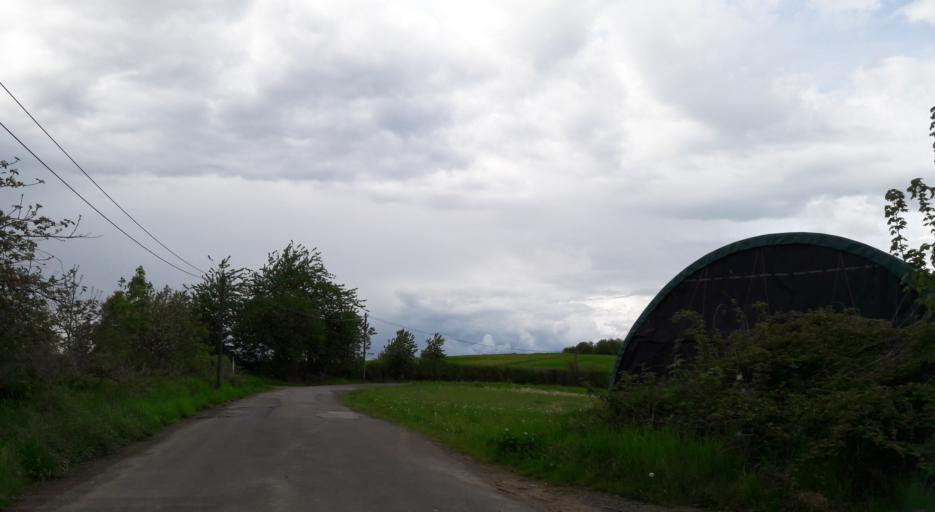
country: DE
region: Saarland
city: Sankt Wendel
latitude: 49.4954
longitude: 7.2076
